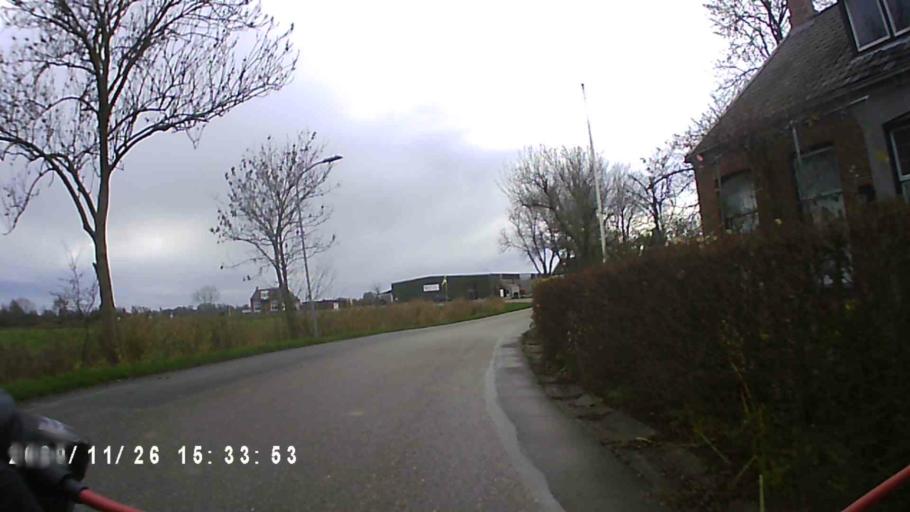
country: NL
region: Groningen
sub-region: Gemeente Slochteren
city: Slochteren
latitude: 53.3104
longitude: 6.7410
